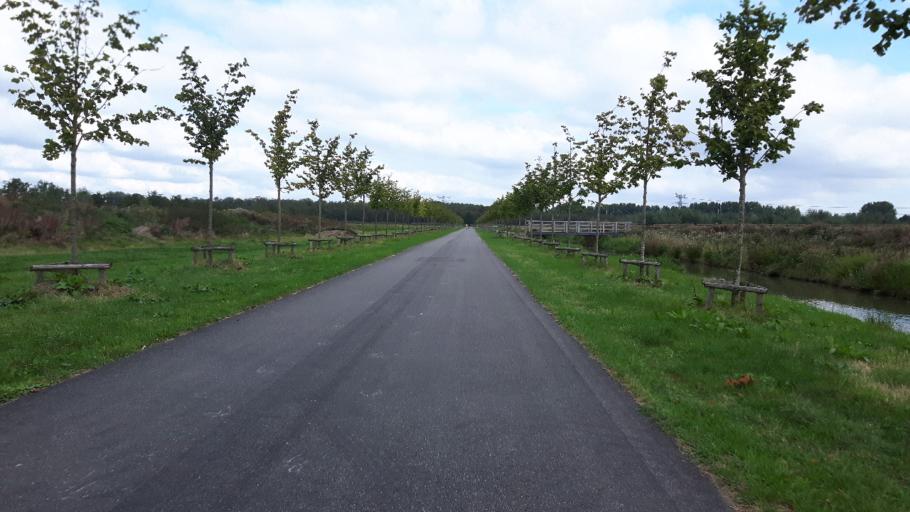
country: NL
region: Utrecht
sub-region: Stichtse Vecht
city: Spechtenkamp
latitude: 52.1245
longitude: 5.0072
